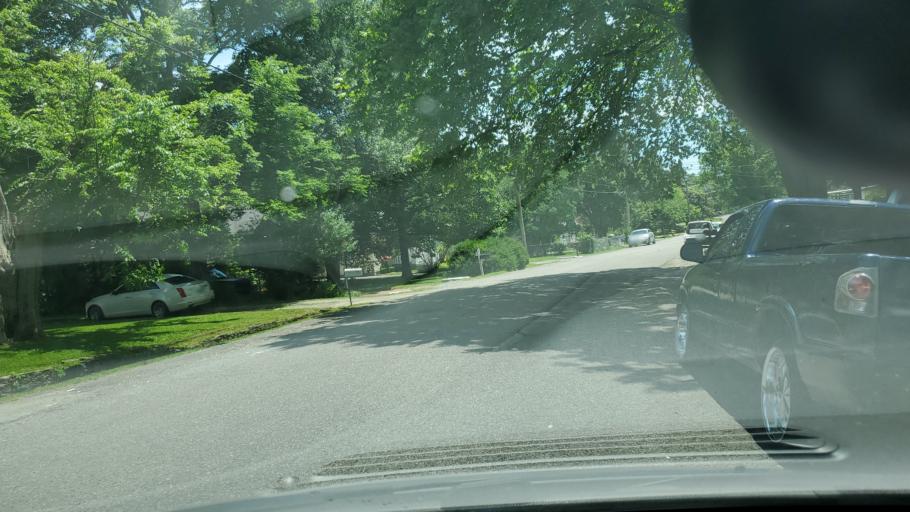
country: US
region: Tennessee
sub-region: Davidson County
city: Nashville
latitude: 36.2133
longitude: -86.7551
